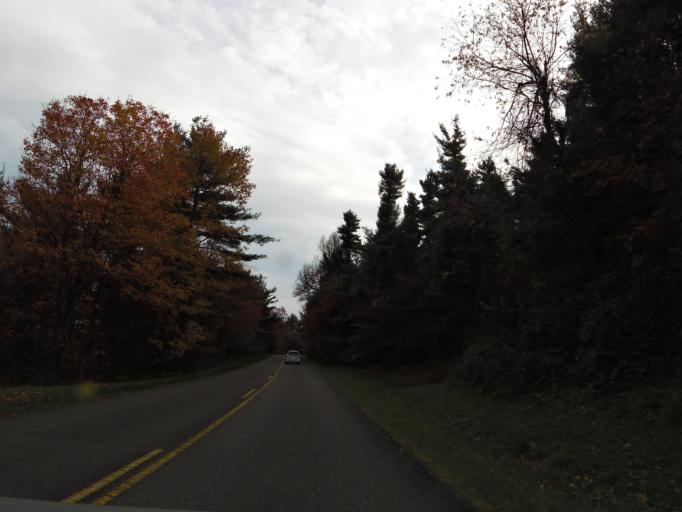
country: US
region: North Carolina
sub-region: Ashe County
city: Jefferson
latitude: 36.3012
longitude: -81.3668
